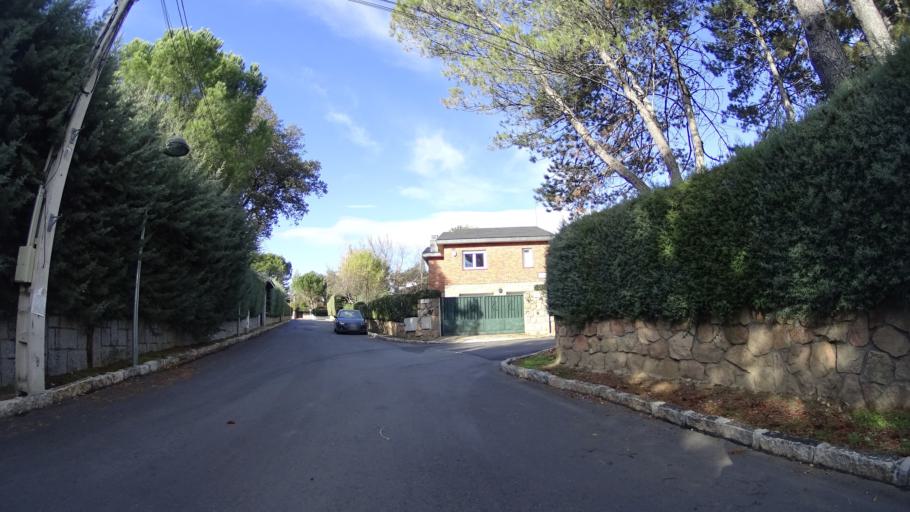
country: ES
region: Madrid
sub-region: Provincia de Madrid
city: Galapagar
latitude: 40.5808
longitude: -4.0244
